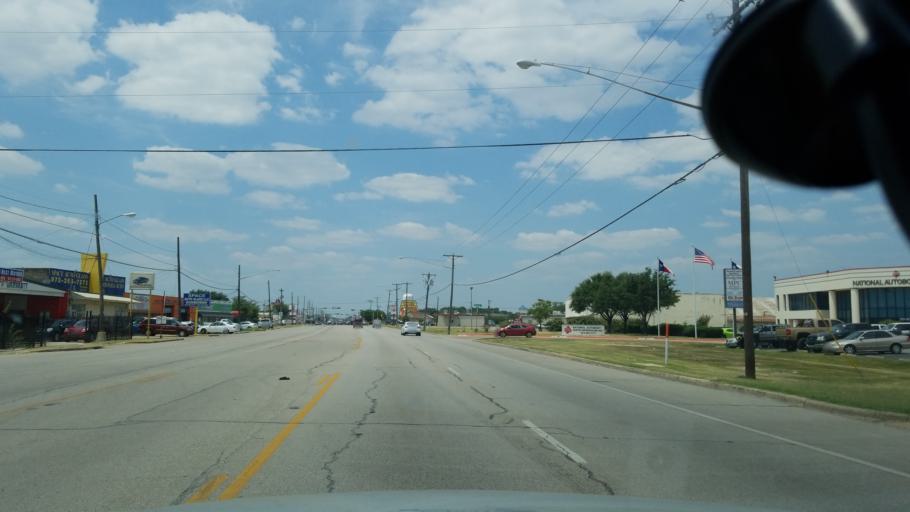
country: US
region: Texas
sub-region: Dallas County
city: Grand Prairie
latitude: 32.7493
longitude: -96.9750
